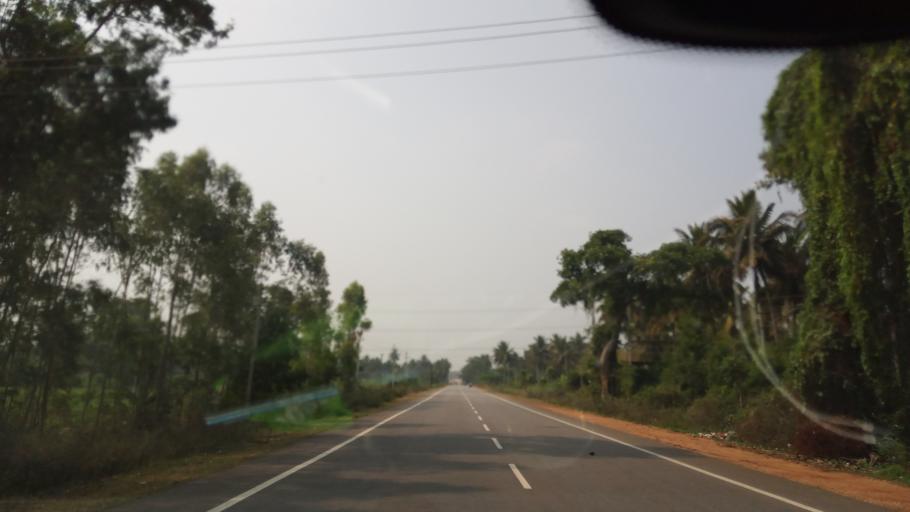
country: IN
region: Karnataka
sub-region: Mandya
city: Pandavapura
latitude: 12.5351
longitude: 76.6706
